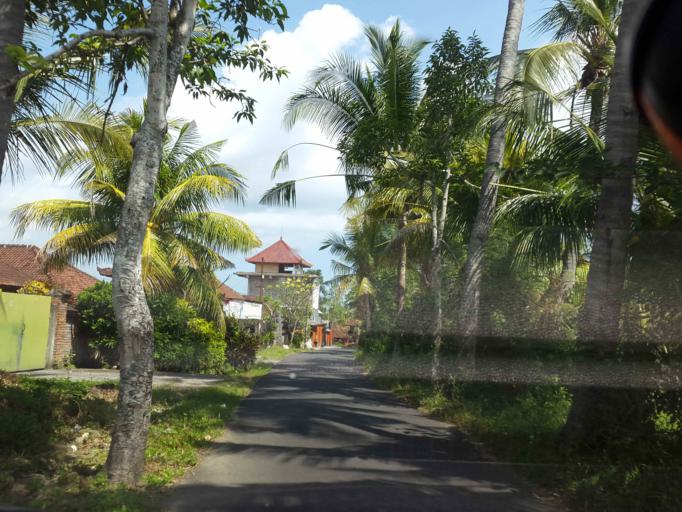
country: ID
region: Bali
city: Klungkung
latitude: -8.5571
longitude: 115.3804
